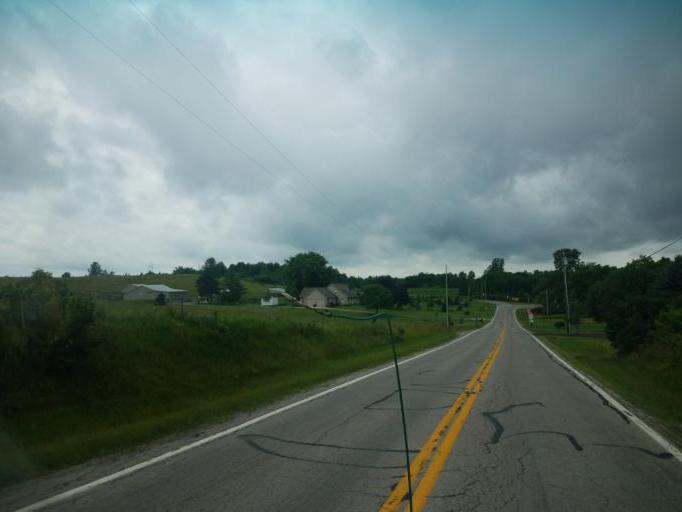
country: US
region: Ohio
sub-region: Logan County
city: Bellefontaine
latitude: 40.3746
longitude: -83.6539
